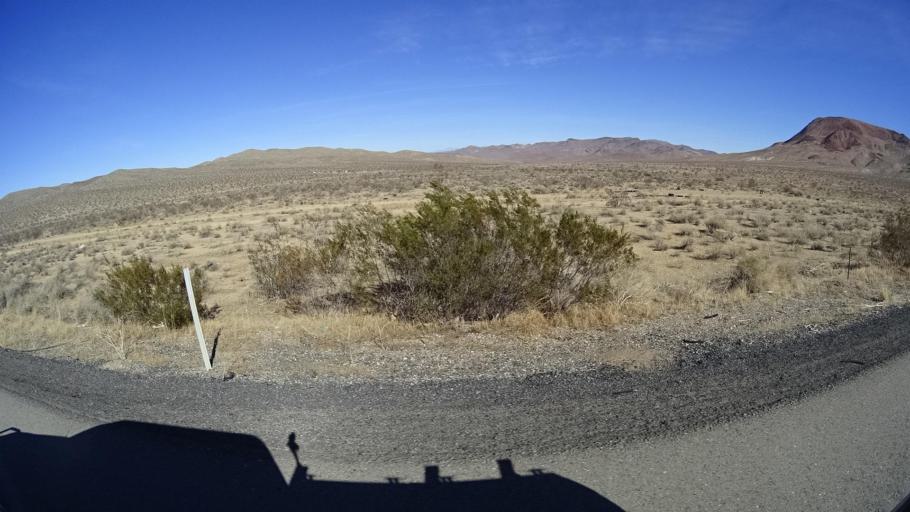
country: US
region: California
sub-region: Kern County
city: Ridgecrest
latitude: 35.3678
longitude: -117.6244
